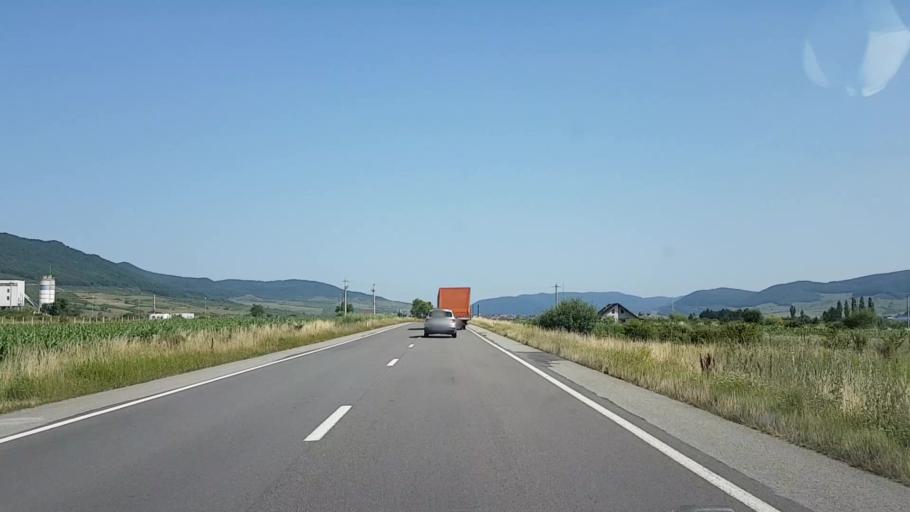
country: RO
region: Bistrita-Nasaud
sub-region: Comuna Sieu-Magherus
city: Sieu-Magherus
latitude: 47.1087
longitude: 24.3476
